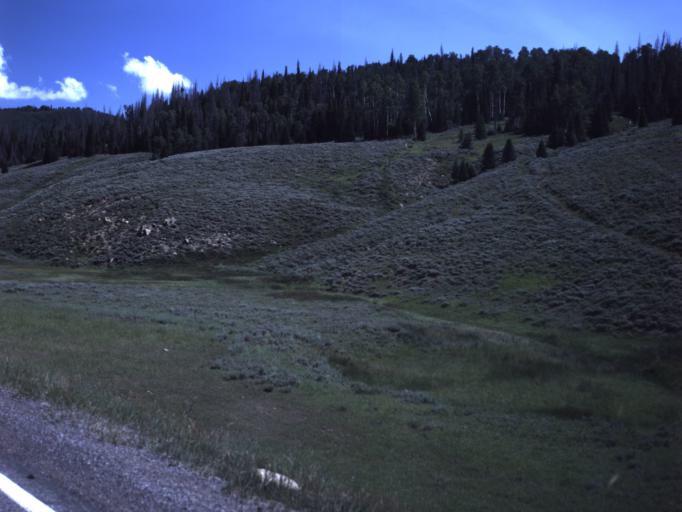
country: US
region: Utah
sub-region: Sanpete County
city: Fairview
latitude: 39.6677
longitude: -111.2441
